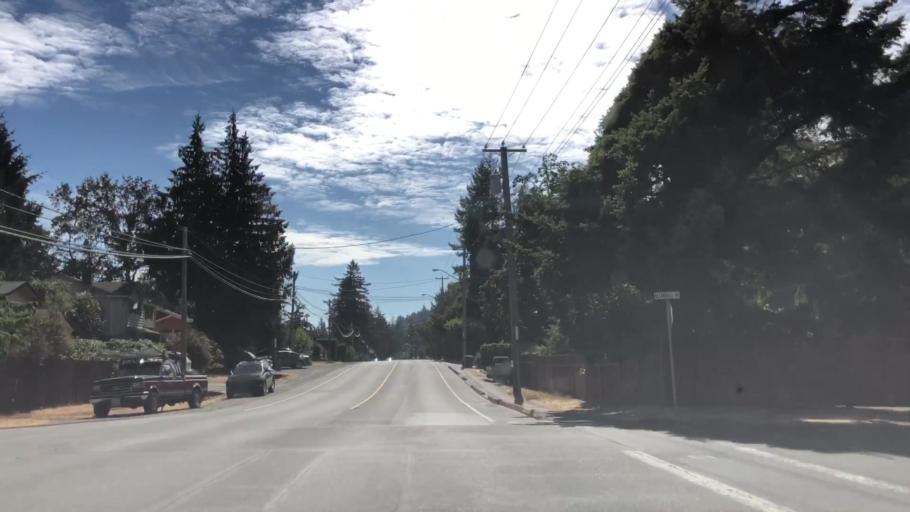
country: CA
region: British Columbia
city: Colwood
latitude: 48.4252
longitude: -123.4912
